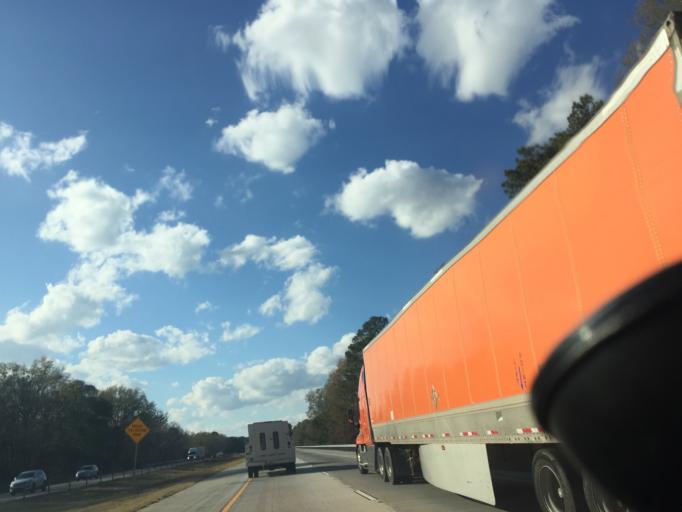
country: US
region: Georgia
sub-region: Laurens County
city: East Dublin
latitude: 32.4824
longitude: -82.8703
